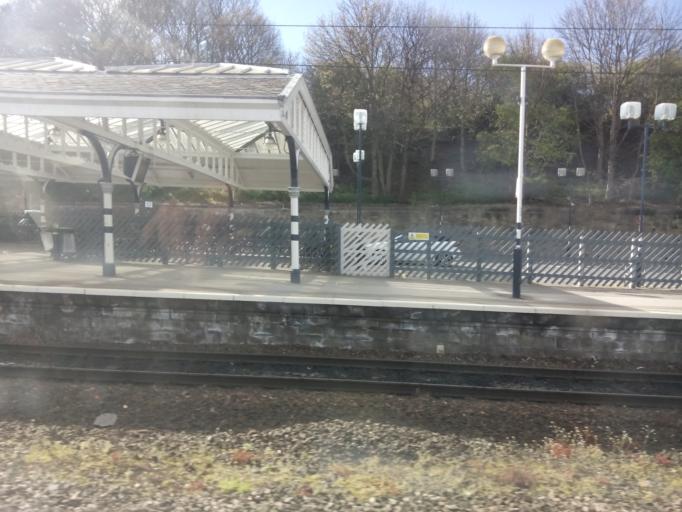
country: GB
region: England
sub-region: County Durham
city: Durham
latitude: 54.7801
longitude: -1.5812
